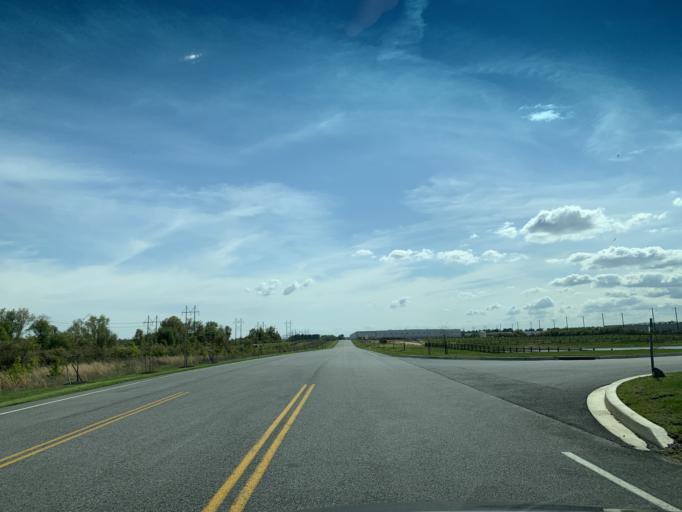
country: US
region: Maryland
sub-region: Harford County
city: Perryman
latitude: 39.4775
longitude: -76.1846
